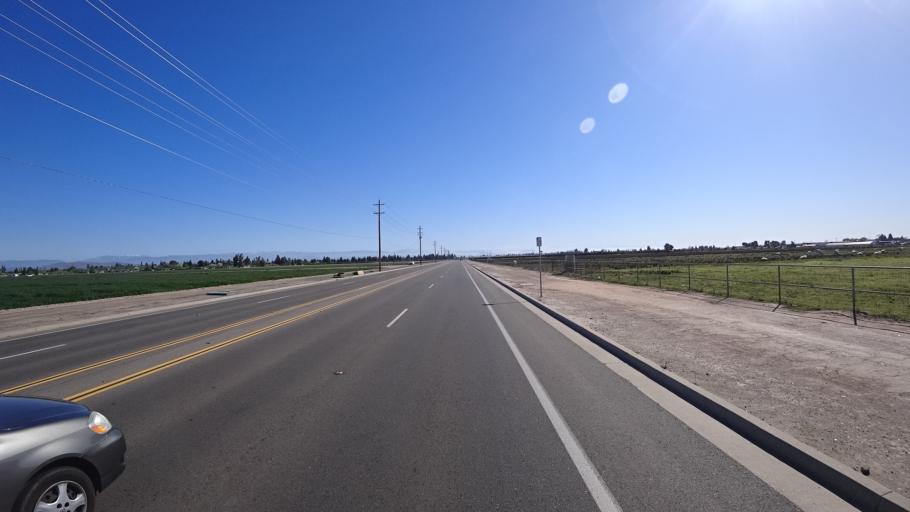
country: US
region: California
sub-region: Fresno County
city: Clovis
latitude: 36.8231
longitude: -119.7424
